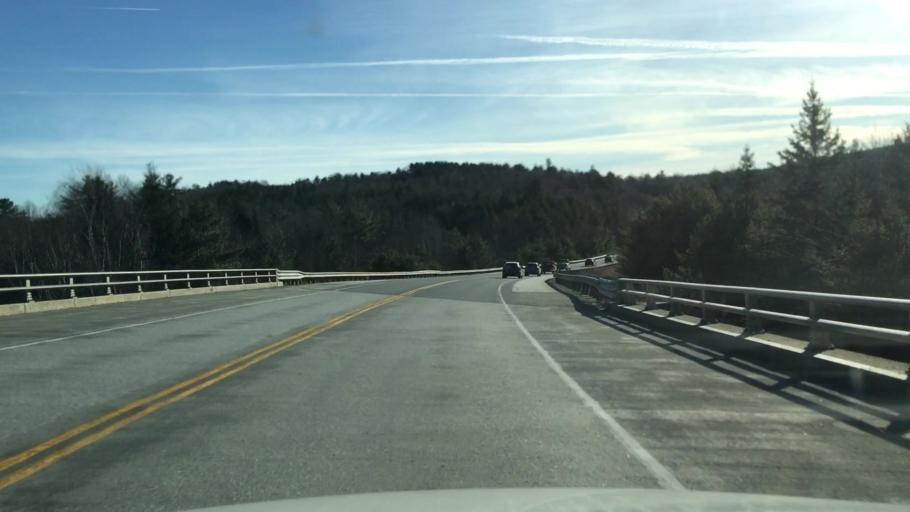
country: US
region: Maine
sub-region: Hancock County
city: Dedham
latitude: 44.6813
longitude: -68.5782
